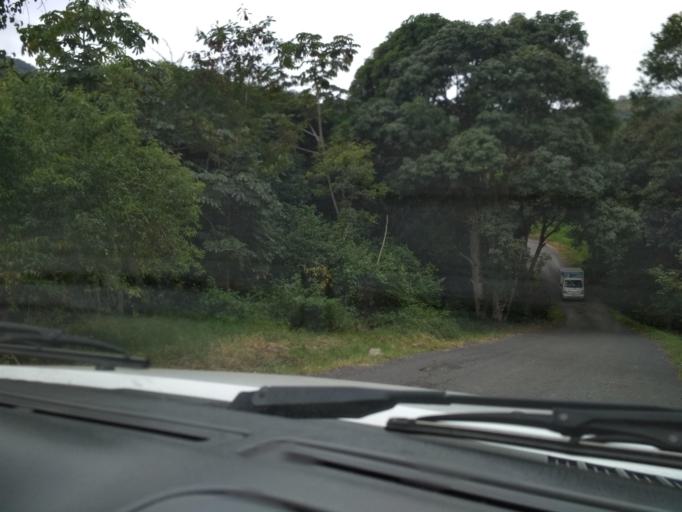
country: MX
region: Veracruz
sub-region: Actopan
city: Trapiche del Rosario
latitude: 19.5642
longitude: -96.7929
